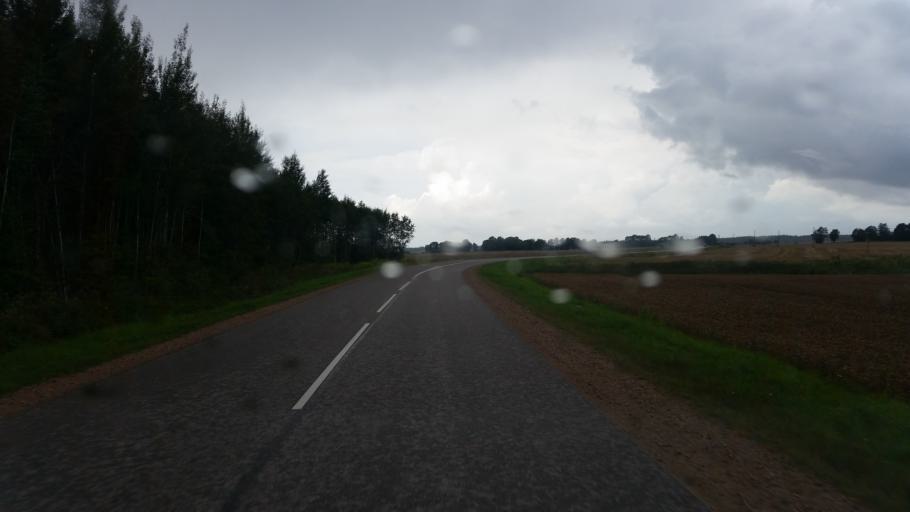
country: LV
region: Vecumnieki
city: Vecumnieki
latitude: 56.4327
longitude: 24.4367
